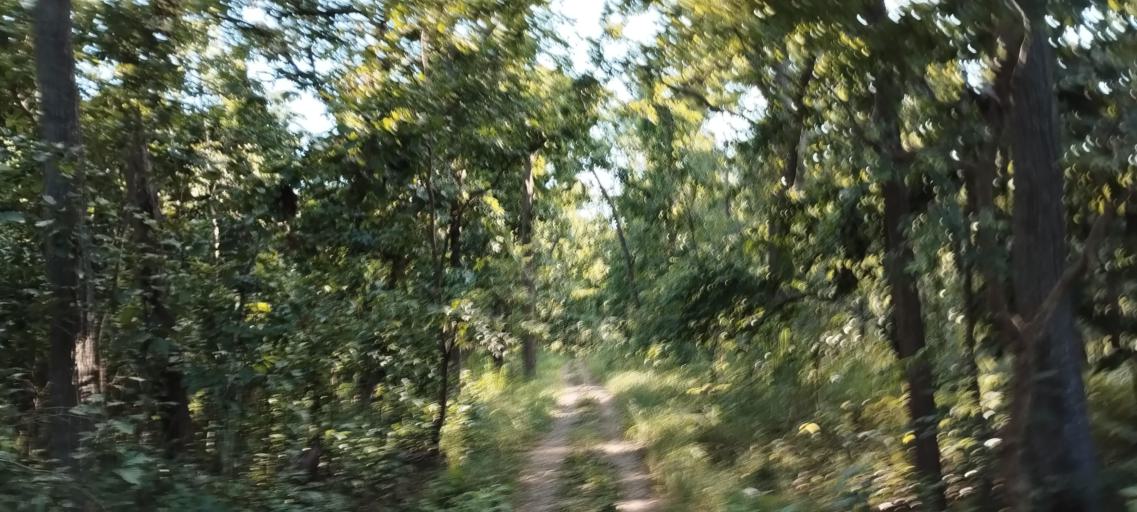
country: NP
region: Far Western
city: Tikapur
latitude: 28.5197
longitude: 81.2761
